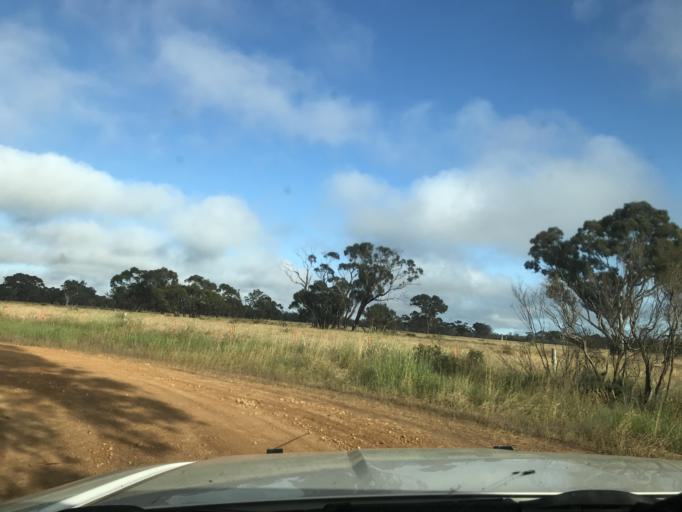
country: AU
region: South Australia
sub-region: Wattle Range
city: Penola
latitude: -37.1805
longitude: 141.1850
